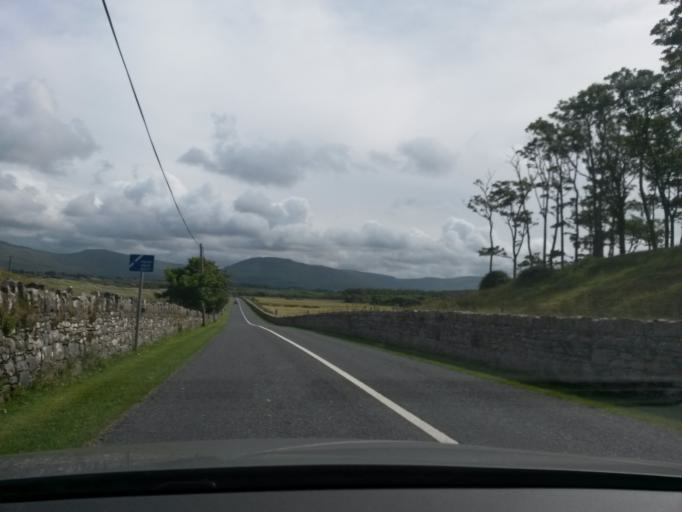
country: IE
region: Connaught
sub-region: County Leitrim
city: Kinlough
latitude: 54.4569
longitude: -8.4558
